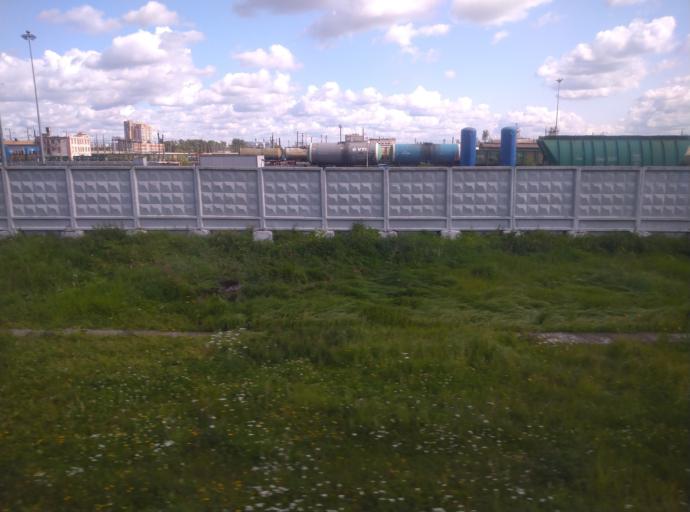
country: RU
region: St.-Petersburg
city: Obukhovo
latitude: 59.8747
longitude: 30.4135
